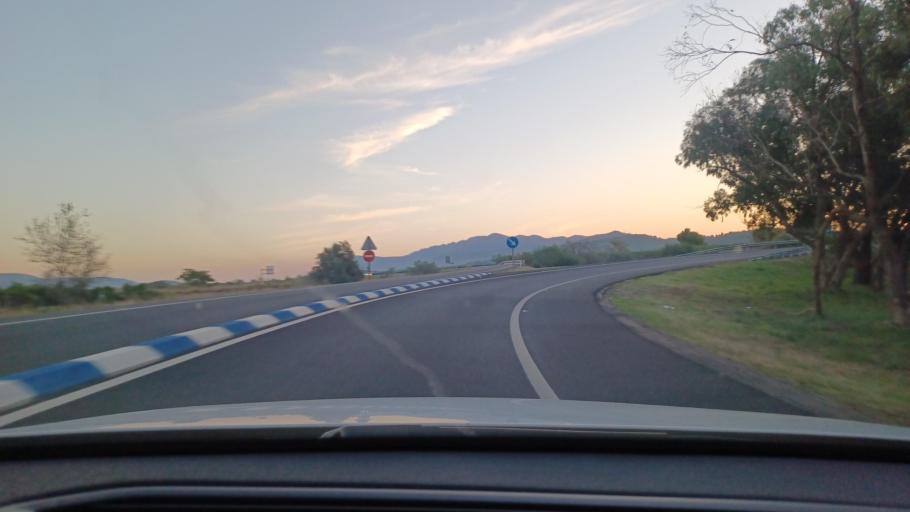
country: ES
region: Catalonia
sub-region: Provincia de Tarragona
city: Ulldecona
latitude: 40.5590
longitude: 0.4259
